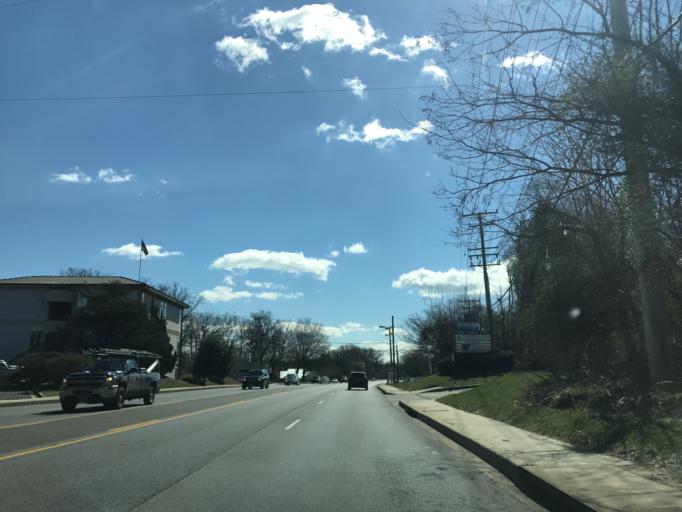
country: US
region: Maryland
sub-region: Anne Arundel County
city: Robinwood
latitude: 38.9649
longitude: -76.5139
